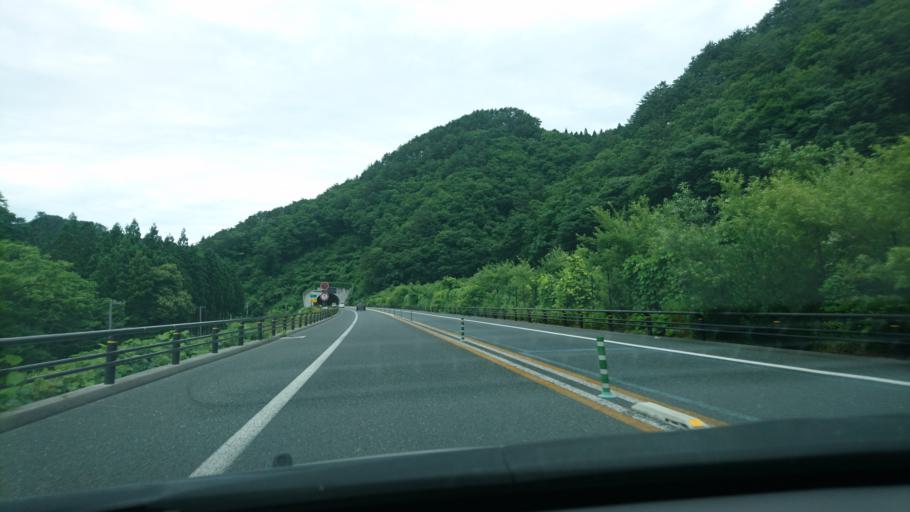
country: JP
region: Iwate
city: Miyako
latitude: 39.8460
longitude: 141.9516
